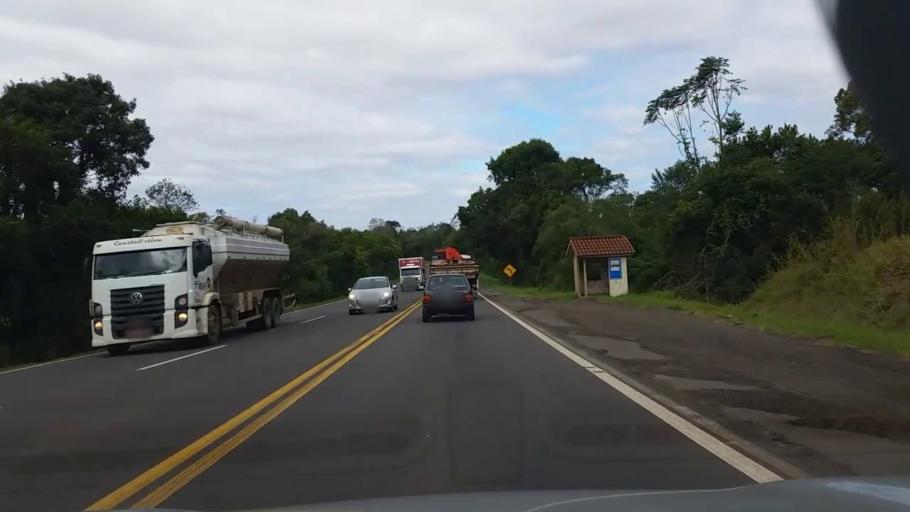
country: BR
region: Rio Grande do Sul
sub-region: Arroio Do Meio
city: Arroio do Meio
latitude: -29.3987
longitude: -52.0411
